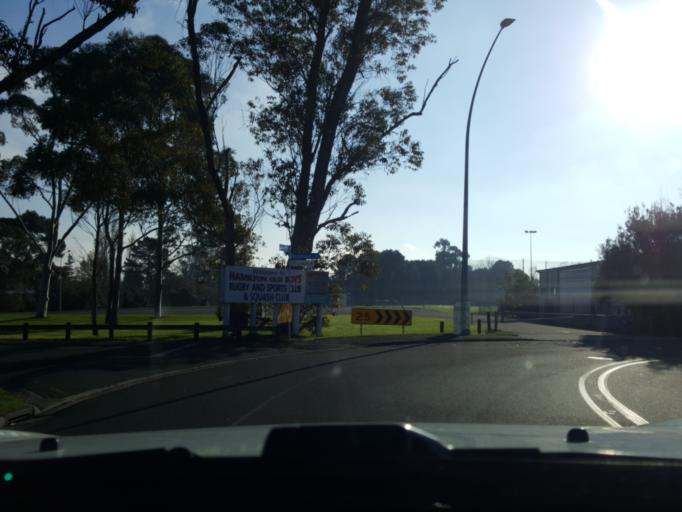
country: NZ
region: Waikato
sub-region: Hamilton City
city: Hamilton
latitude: -37.7788
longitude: 175.2671
